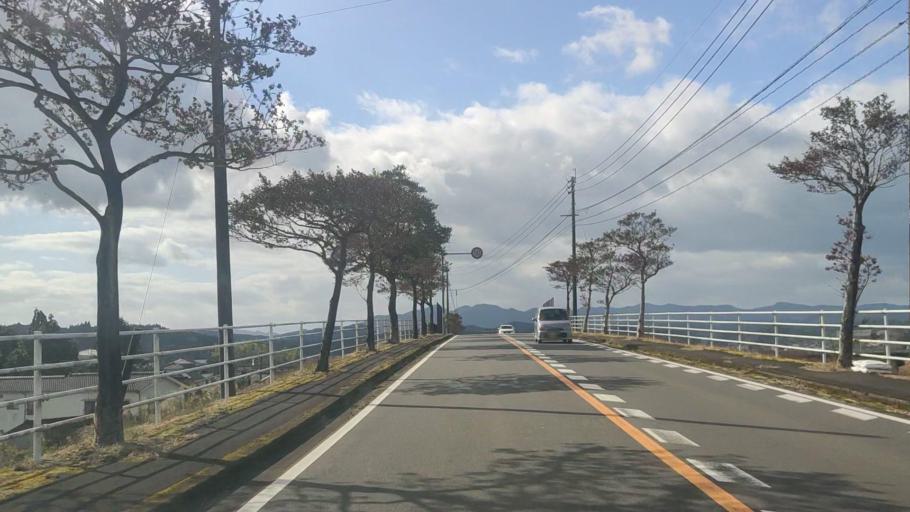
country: JP
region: Kagoshima
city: Okuchi-shinohara
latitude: 31.9563
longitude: 130.7279
